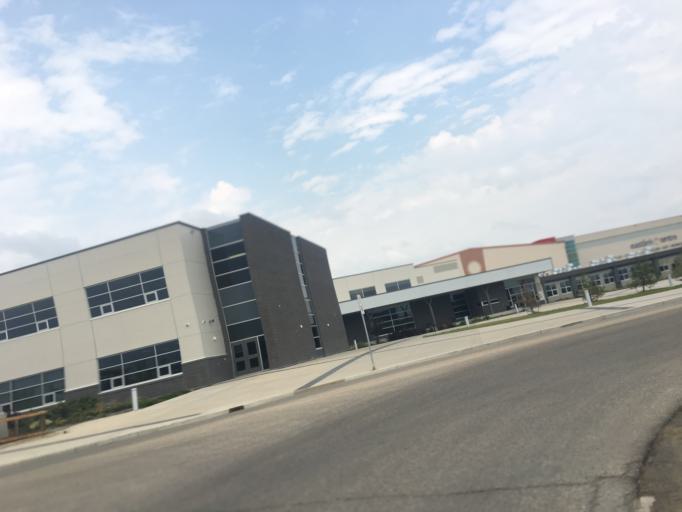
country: CA
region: Alberta
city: Grande Prairie
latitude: 55.1424
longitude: -118.8145
